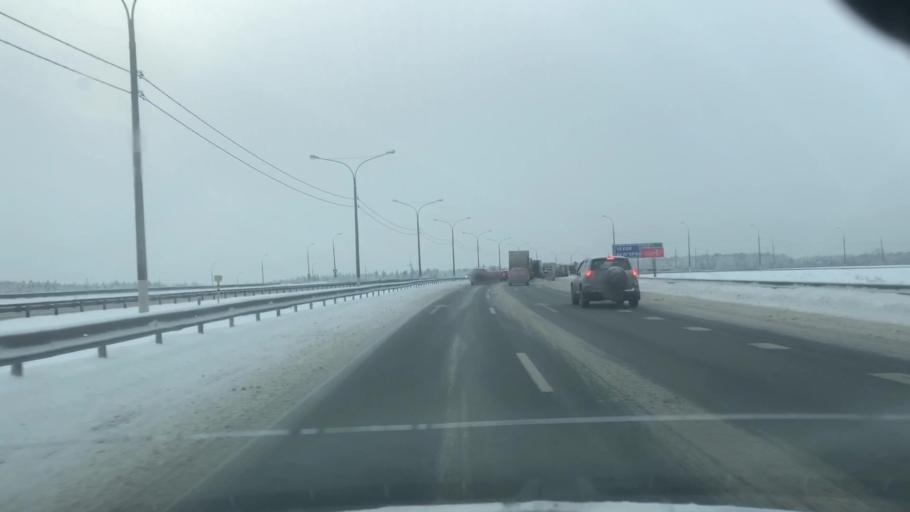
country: RU
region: Moskovskaya
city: Mikhnevo
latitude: 55.0805
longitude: 37.9362
